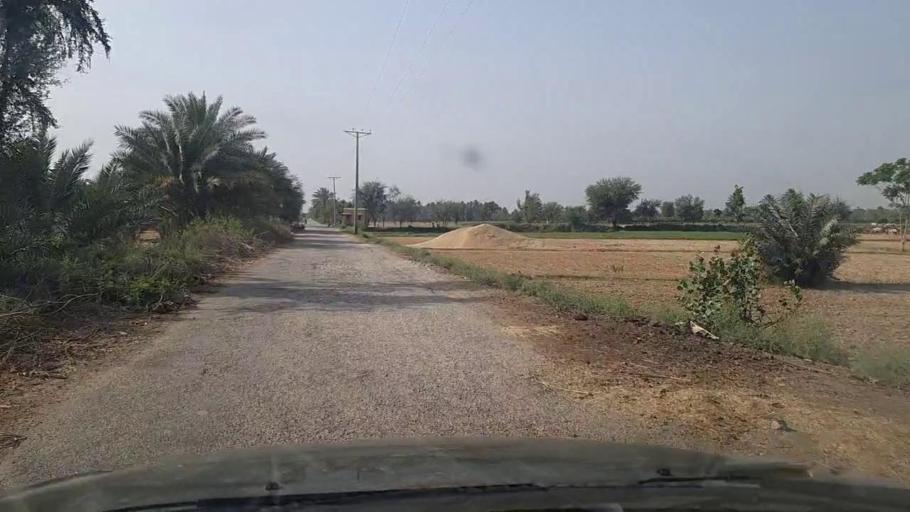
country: PK
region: Sindh
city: Kot Diji
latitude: 27.2804
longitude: 68.6507
